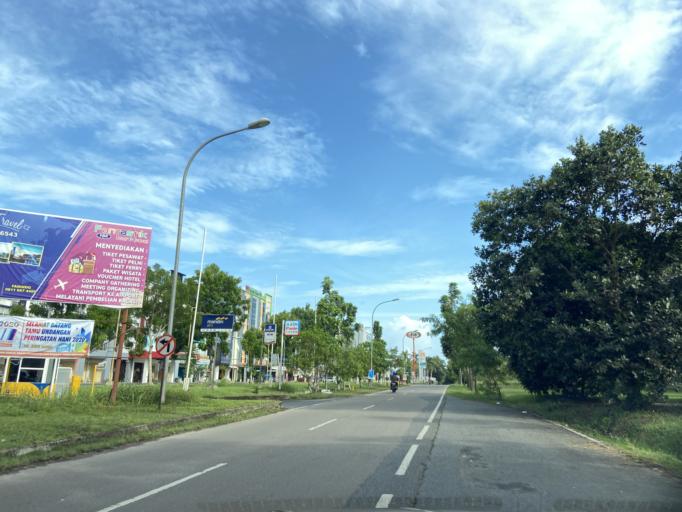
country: SG
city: Singapore
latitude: 1.1062
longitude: 104.0308
